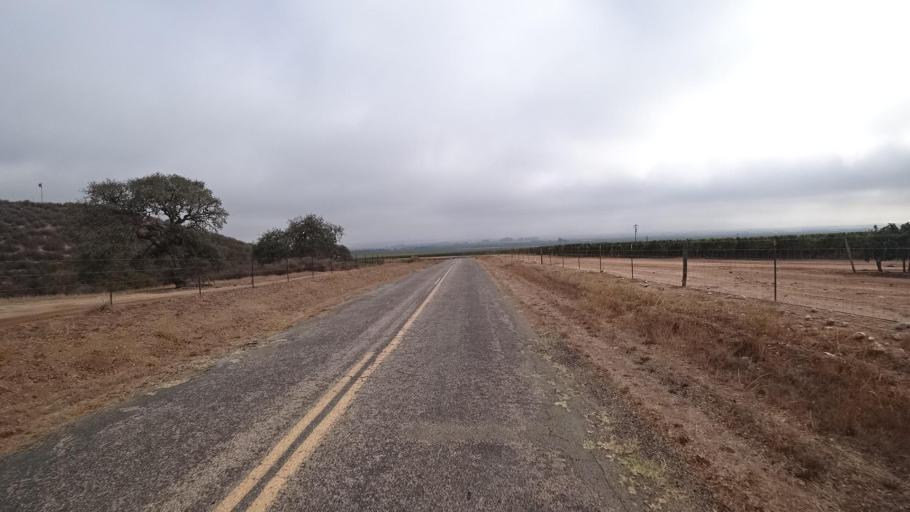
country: US
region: California
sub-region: Monterey County
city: Soledad
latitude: 36.3496
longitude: -121.3370
